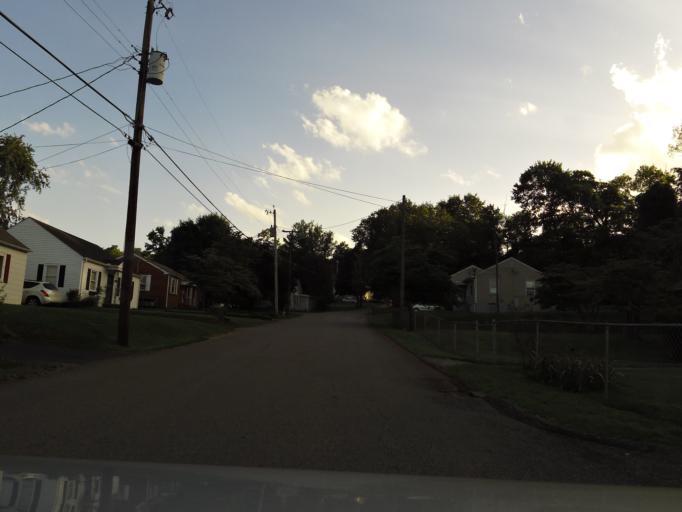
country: US
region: Tennessee
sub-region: Knox County
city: Knoxville
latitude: 35.9556
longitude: -83.9040
